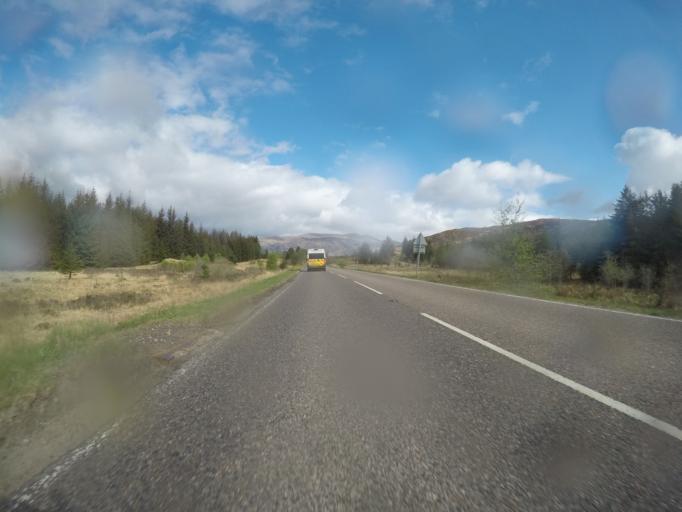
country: GB
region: Scotland
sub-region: Highland
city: Spean Bridge
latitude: 56.9071
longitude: -4.9445
